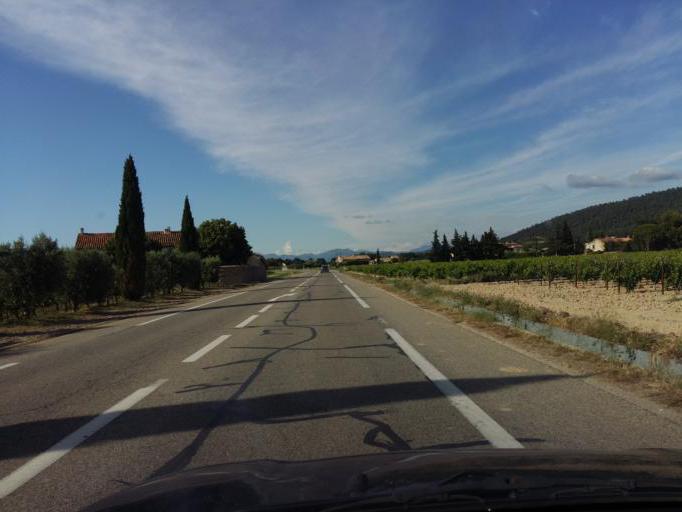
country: FR
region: Provence-Alpes-Cote d'Azur
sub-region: Departement du Vaucluse
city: Sablet
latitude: 44.2160
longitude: 5.0062
